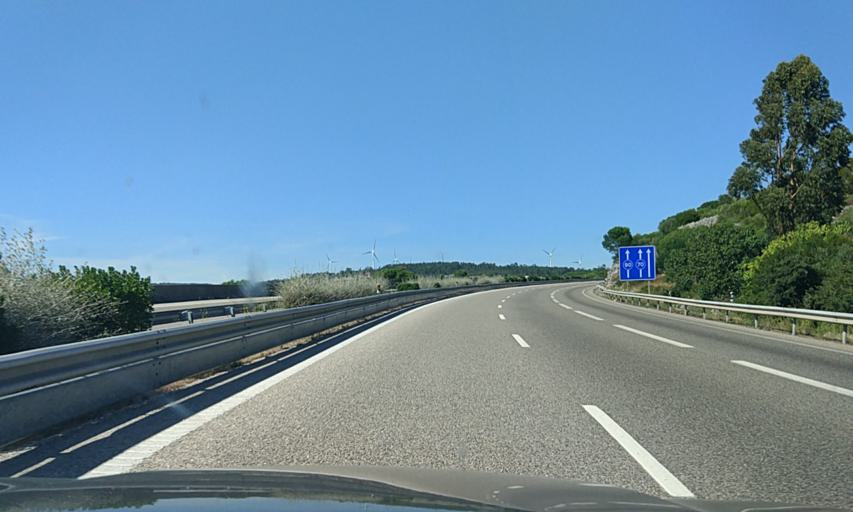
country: PT
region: Santarem
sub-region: Alcanena
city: Alcanena
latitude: 39.5151
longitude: -8.6695
